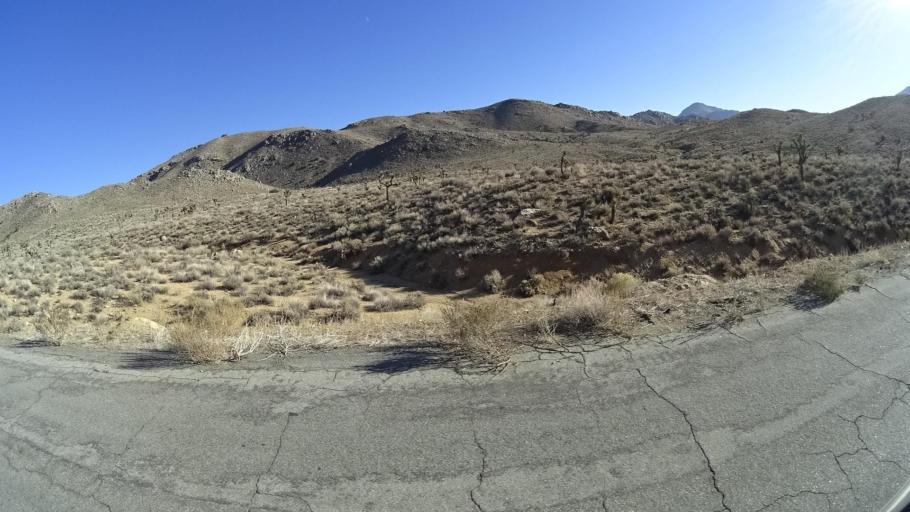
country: US
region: California
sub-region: Kern County
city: Weldon
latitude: 35.5252
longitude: -118.2006
